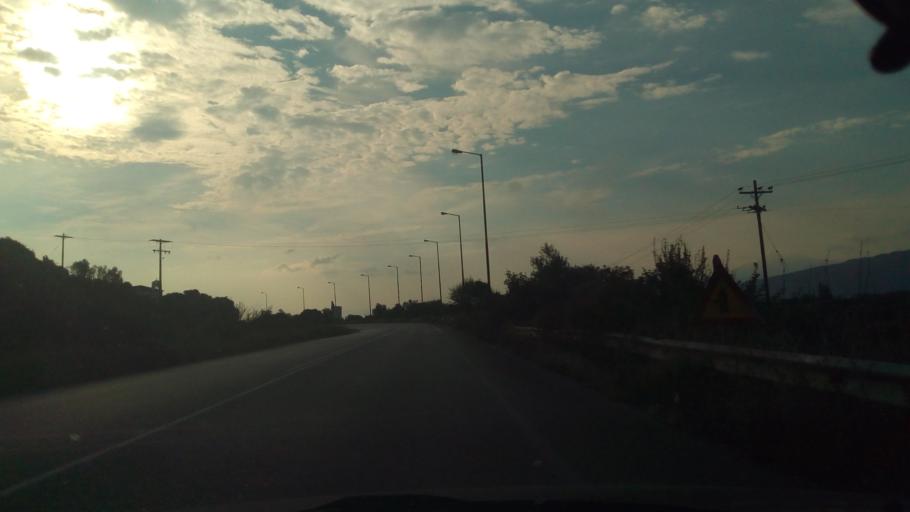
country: GR
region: West Greece
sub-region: Nomos Aitolias kai Akarnanias
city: Nafpaktos
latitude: 38.4048
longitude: 21.9133
